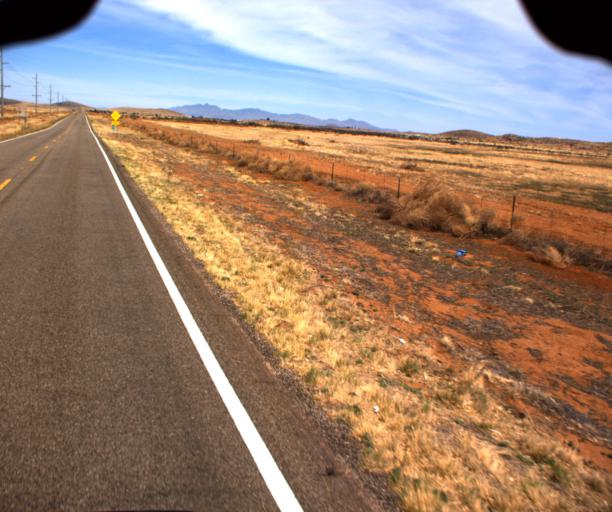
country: US
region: Arizona
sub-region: Cochise County
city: Tombstone
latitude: 31.8517
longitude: -109.6951
